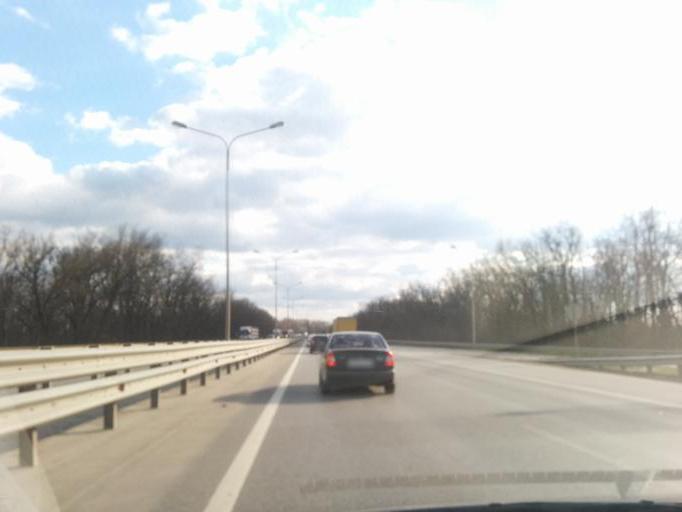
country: RU
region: Rostov
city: Grushevskaya
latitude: 47.3761
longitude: 39.9061
